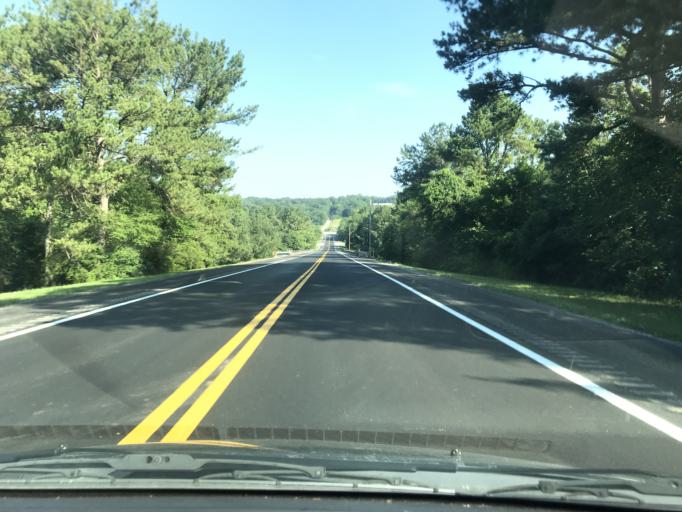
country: US
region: Tennessee
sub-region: Loudon County
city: Loudon
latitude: 35.7822
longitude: -84.3427
